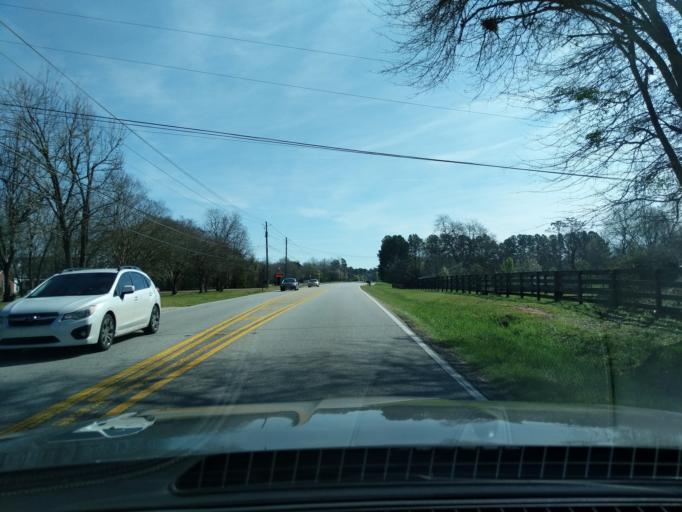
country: US
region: Georgia
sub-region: Columbia County
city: Evans
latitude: 33.5304
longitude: -82.1615
